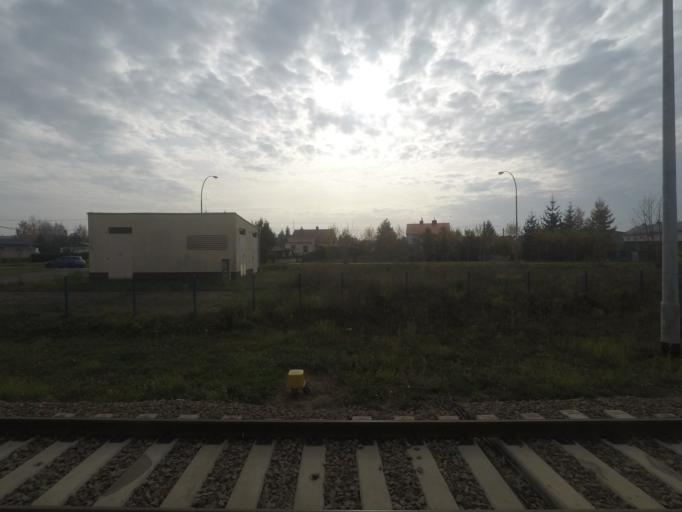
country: PL
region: Subcarpathian Voivodeship
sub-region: Powiat ropczycko-sedziszowski
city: Ostrow
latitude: 50.0790
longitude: 21.5853
